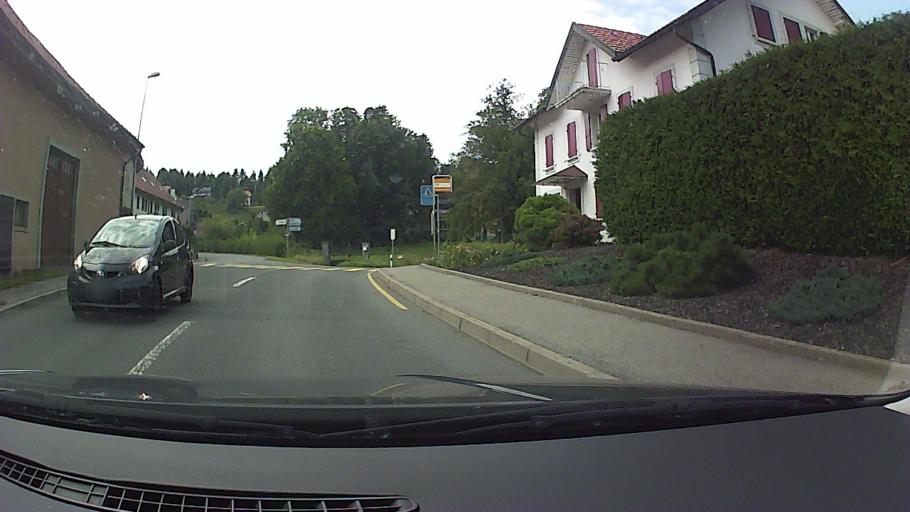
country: CH
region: Fribourg
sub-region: Veveyse District
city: Chatel-Saint-Denis
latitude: 46.5892
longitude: 6.9218
